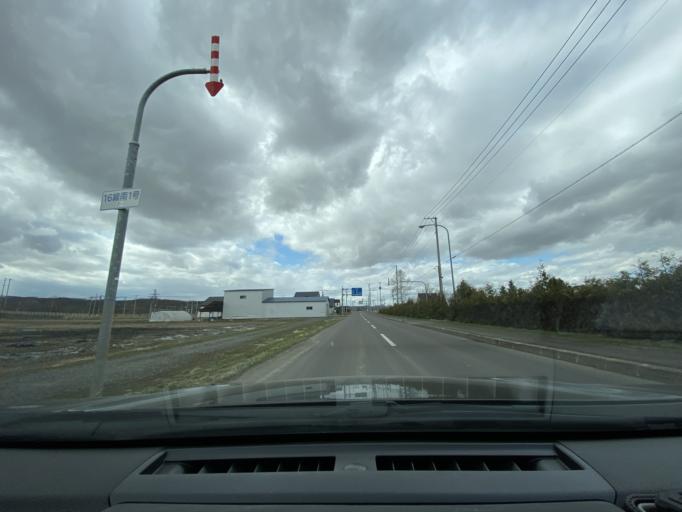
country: JP
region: Hokkaido
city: Nayoro
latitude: 44.1307
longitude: 142.4872
